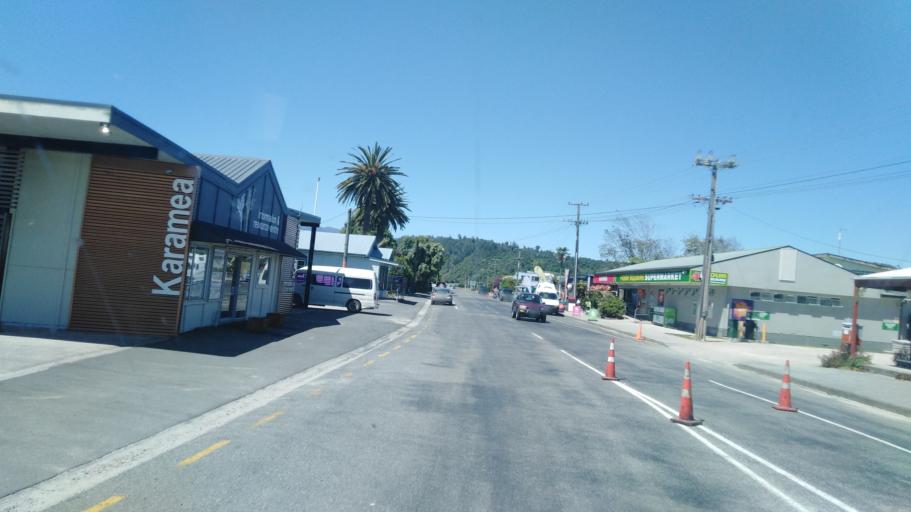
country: NZ
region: West Coast
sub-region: Buller District
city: Westport
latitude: -41.2511
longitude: 172.1285
